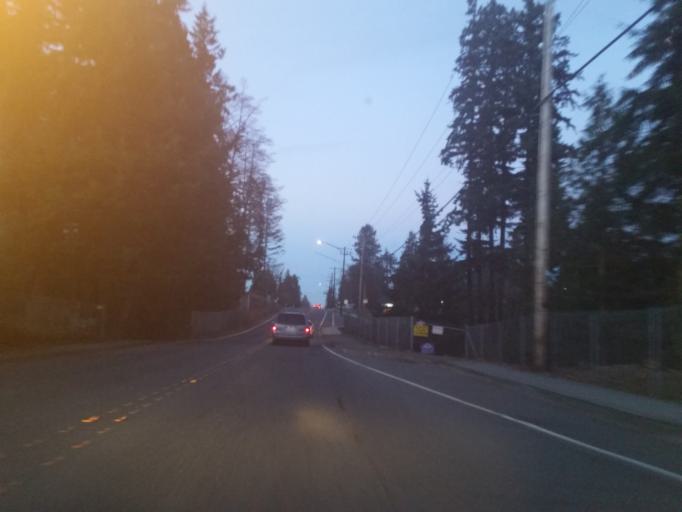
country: US
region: Washington
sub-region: Snohomish County
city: Lynnwood
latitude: 47.8481
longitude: -122.3036
